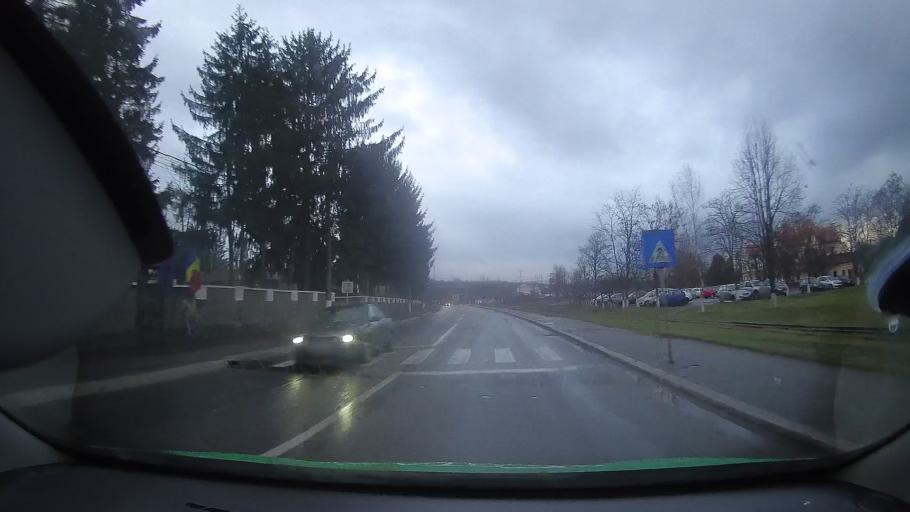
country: RO
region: Hunedoara
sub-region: Municipiul Brad
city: Brad
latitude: 46.1364
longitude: 22.7805
